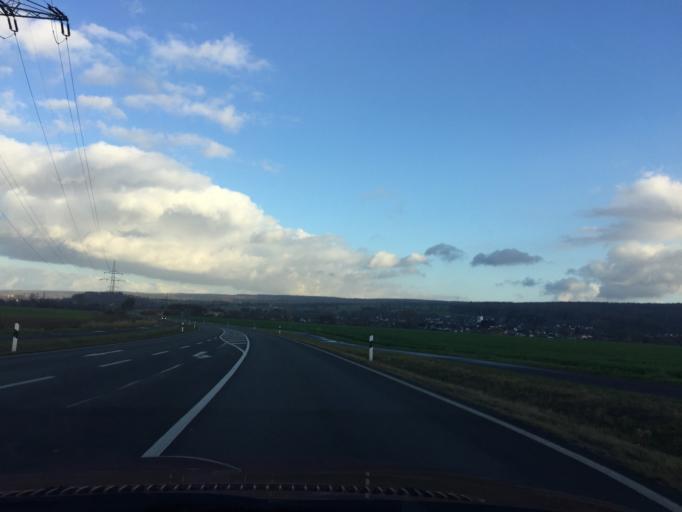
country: DE
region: North Rhine-Westphalia
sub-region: Regierungsbezirk Detmold
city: Hoexter
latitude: 51.7958
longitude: 9.4054
